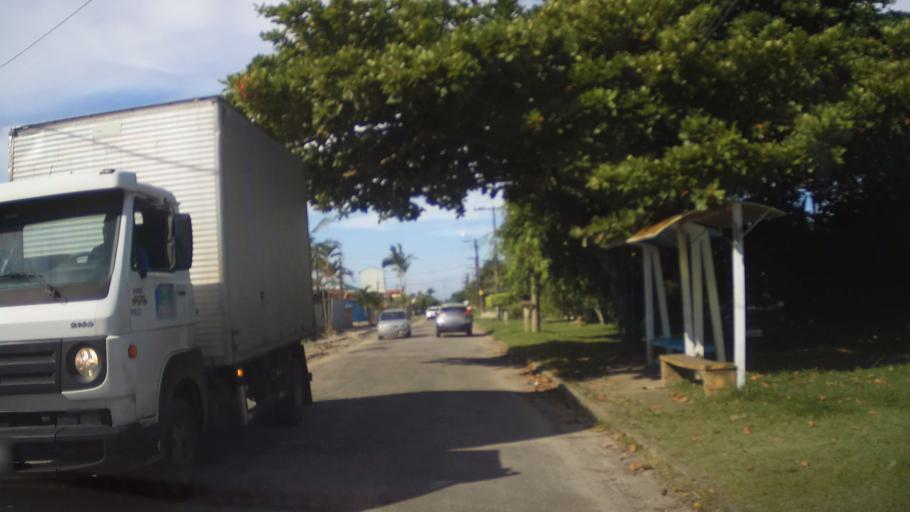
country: BR
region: Sao Paulo
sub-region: Itanhaem
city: Itanhaem
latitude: -24.2054
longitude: -46.8336
